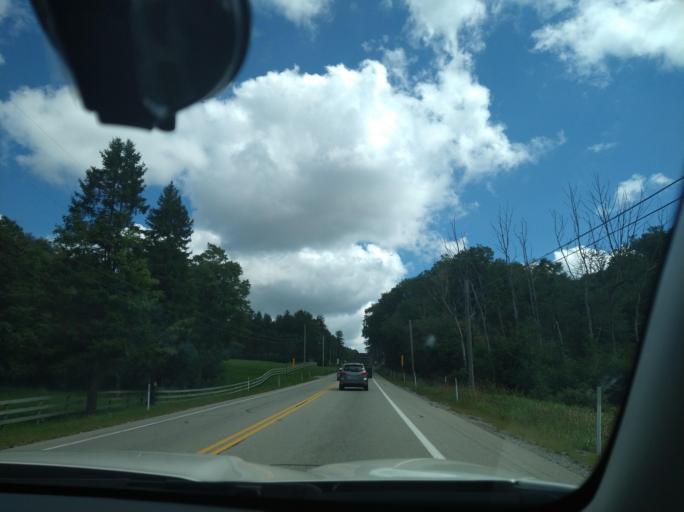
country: US
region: Pennsylvania
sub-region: Westmoreland County
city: Ligonier
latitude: 40.0685
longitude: -79.2750
